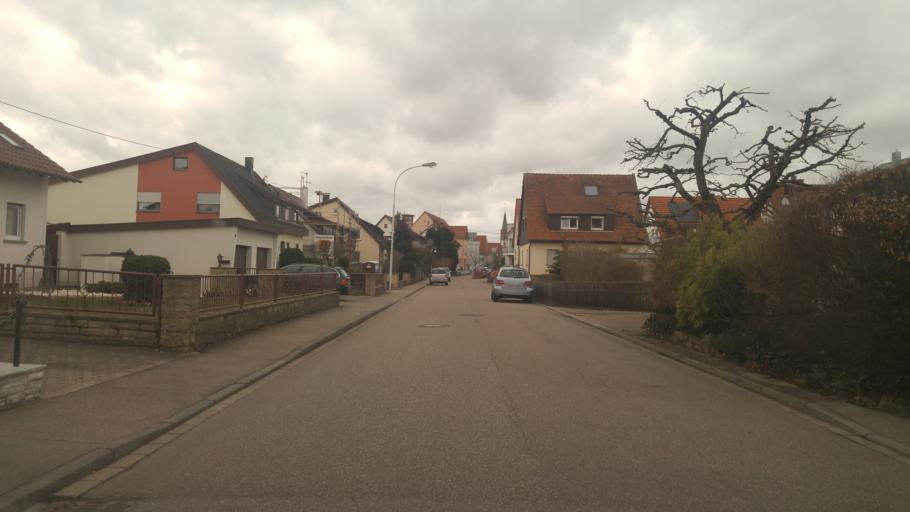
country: DE
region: Baden-Wuerttemberg
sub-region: Regierungsbezirk Stuttgart
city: Rutesheim
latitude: 48.8091
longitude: 8.9497
